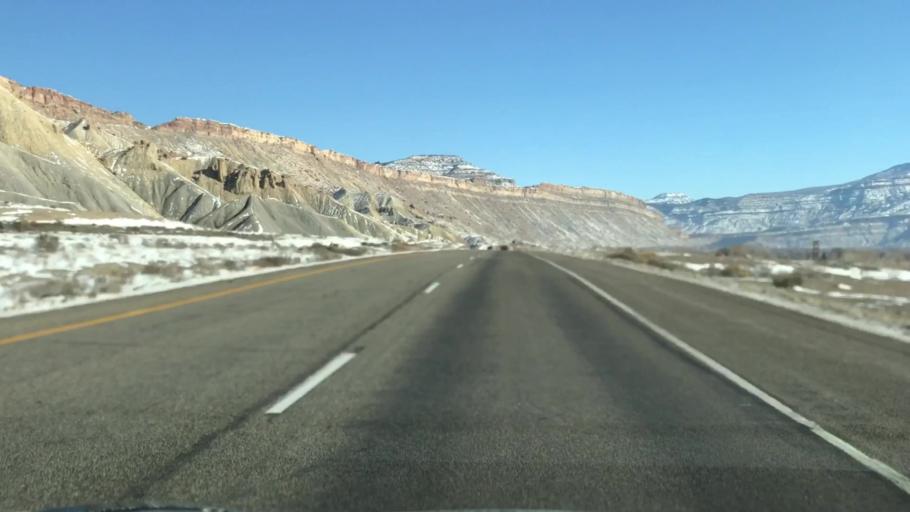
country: US
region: Colorado
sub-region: Mesa County
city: Clifton
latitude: 39.1125
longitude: -108.4097
